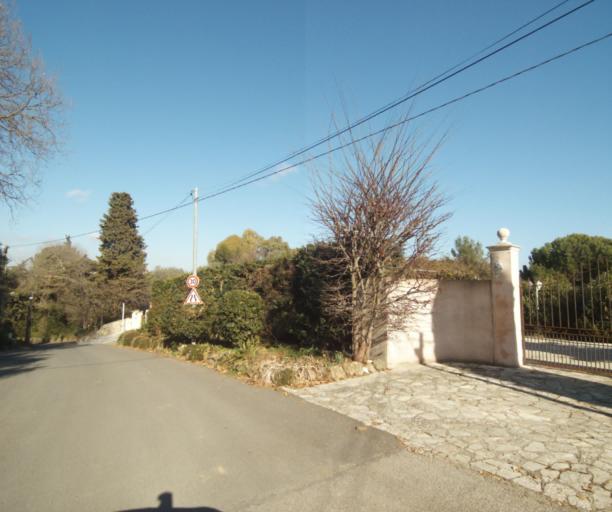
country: FR
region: Provence-Alpes-Cote d'Azur
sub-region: Departement des Alpes-Maritimes
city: Biot
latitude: 43.6129
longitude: 7.1036
